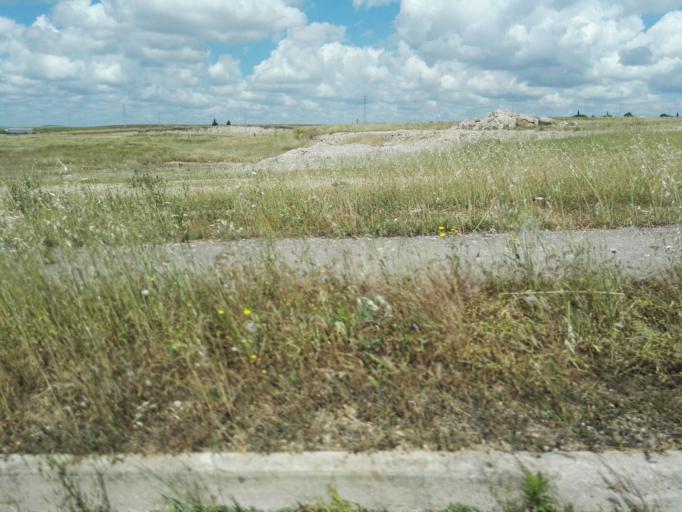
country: ES
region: Extremadura
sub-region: Provincia de Badajoz
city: Badajoz
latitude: 38.9032
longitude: -6.9942
